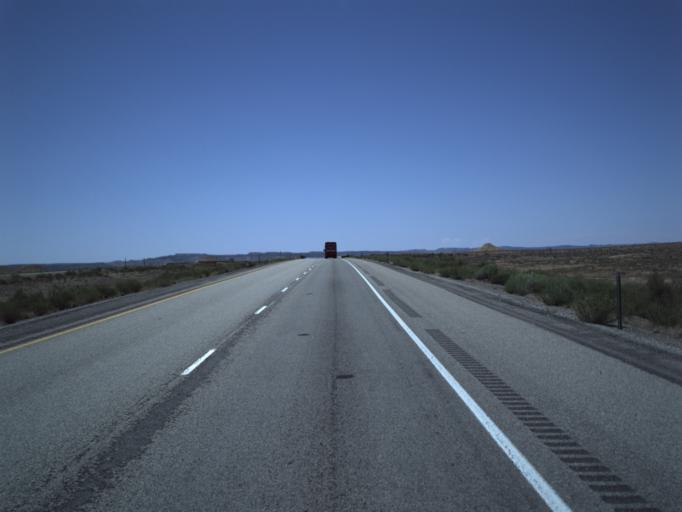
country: US
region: Utah
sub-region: Grand County
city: Moab
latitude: 38.9574
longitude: -109.3848
